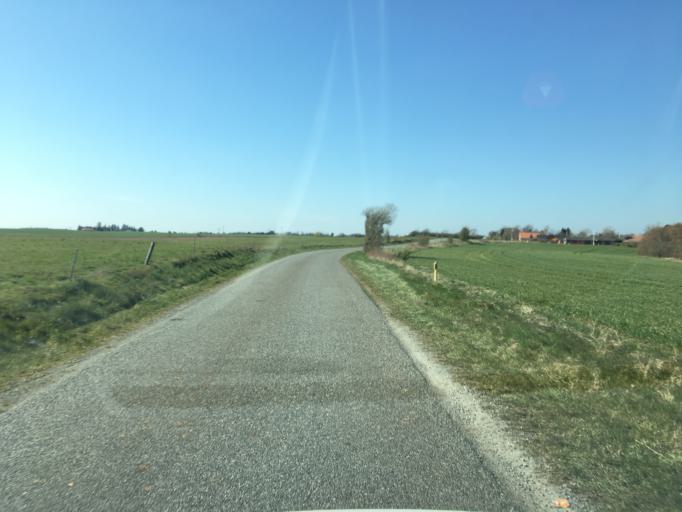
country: DK
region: South Denmark
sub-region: Aabenraa Kommune
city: Krusa
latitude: 54.9285
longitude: 9.4152
